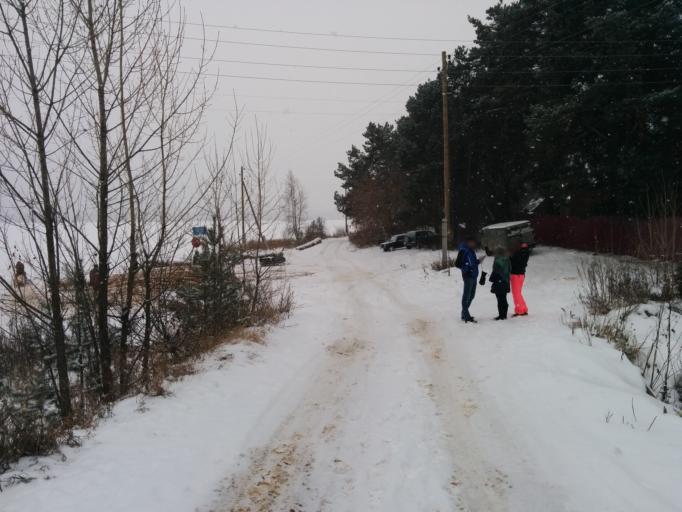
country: RU
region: Perm
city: Okhansk
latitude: 57.7074
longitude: 55.4193
